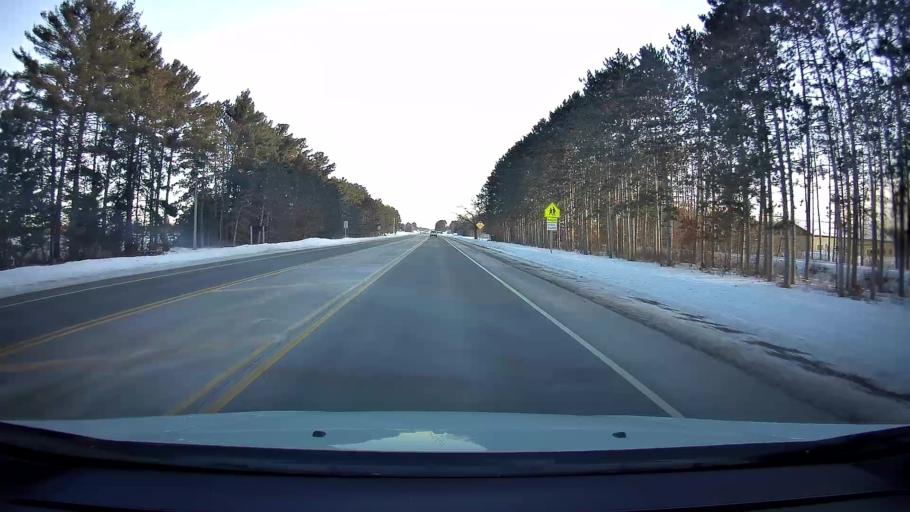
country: US
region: Wisconsin
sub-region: Washburn County
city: Shell Lake
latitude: 45.7270
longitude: -91.9336
